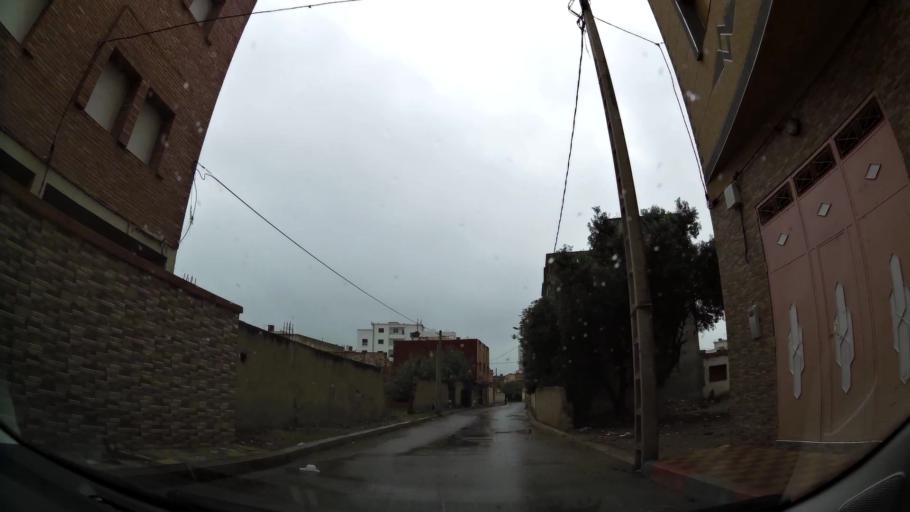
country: MA
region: Oriental
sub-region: Nador
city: Nador
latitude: 35.1598
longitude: -2.9528
